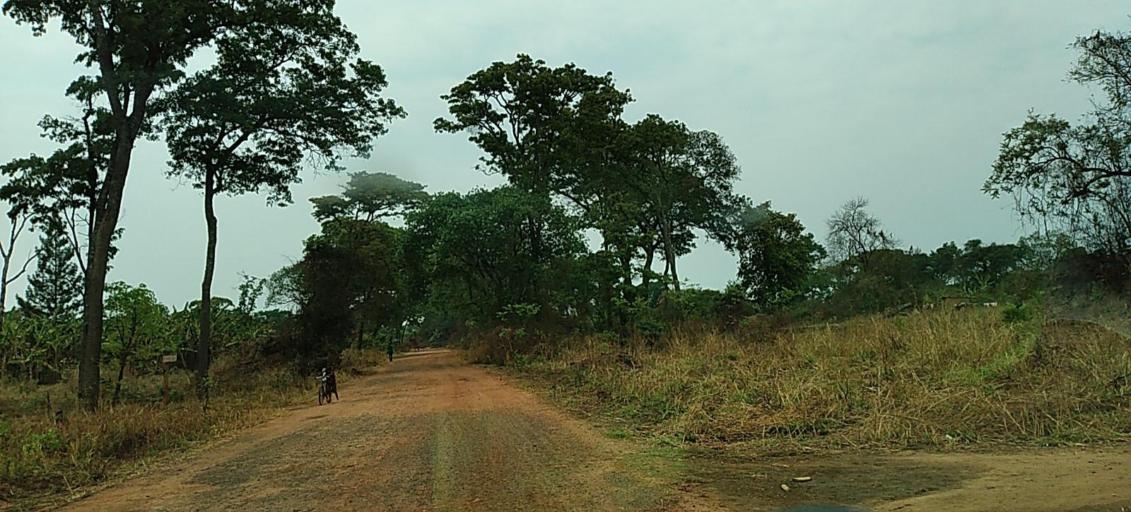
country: ZM
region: North-Western
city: Solwezi
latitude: -12.3405
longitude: 26.5256
